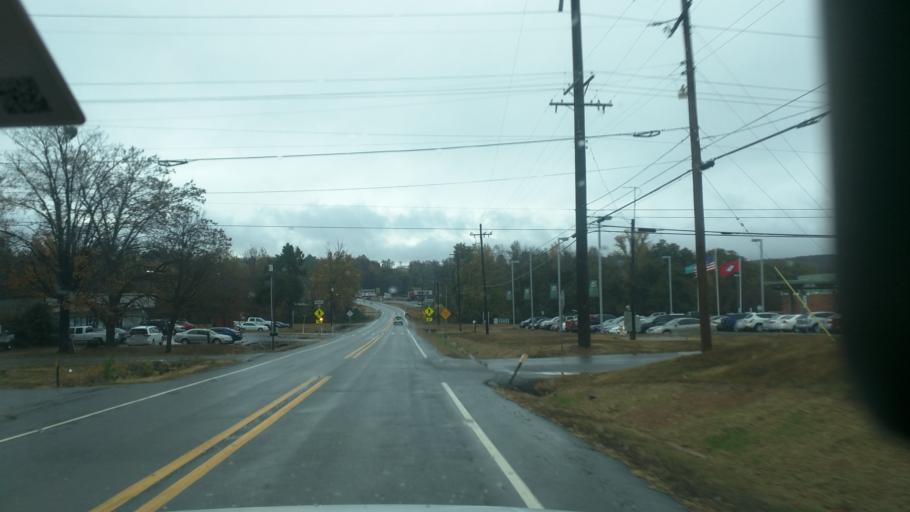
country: US
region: Arkansas
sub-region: Franklin County
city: Ozark
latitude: 35.4967
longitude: -93.8435
